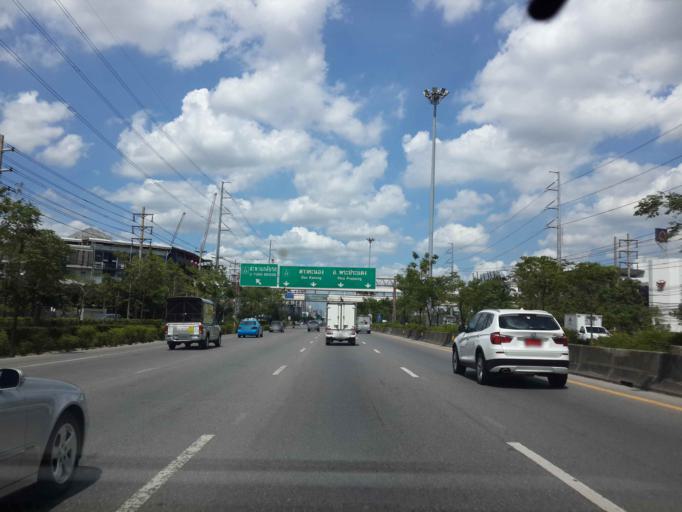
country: TH
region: Bangkok
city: Bang Khun Thian
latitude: 13.6685
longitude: 100.4493
